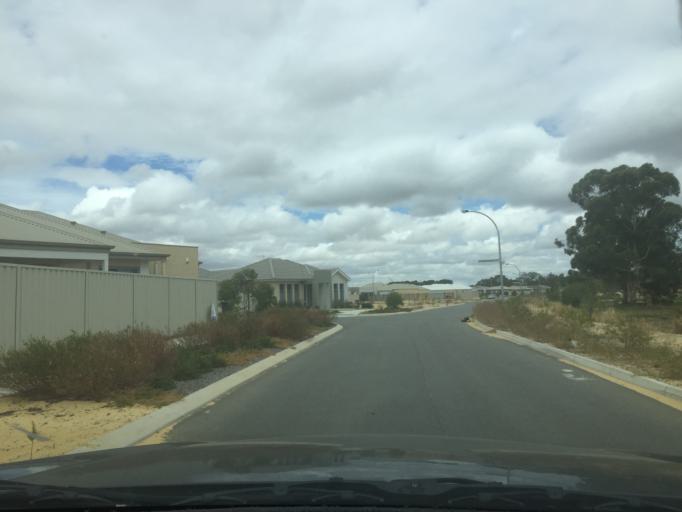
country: AU
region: Western Australia
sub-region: Armadale
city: Harrisdale
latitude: -32.1356
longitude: 115.9063
